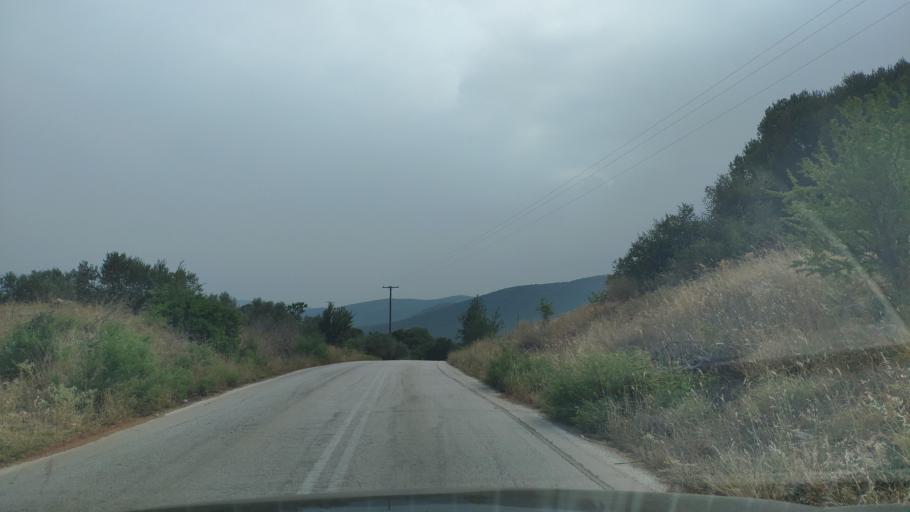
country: GR
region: Peloponnese
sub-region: Nomos Argolidos
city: Palaia Epidavros
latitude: 37.5861
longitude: 23.1563
